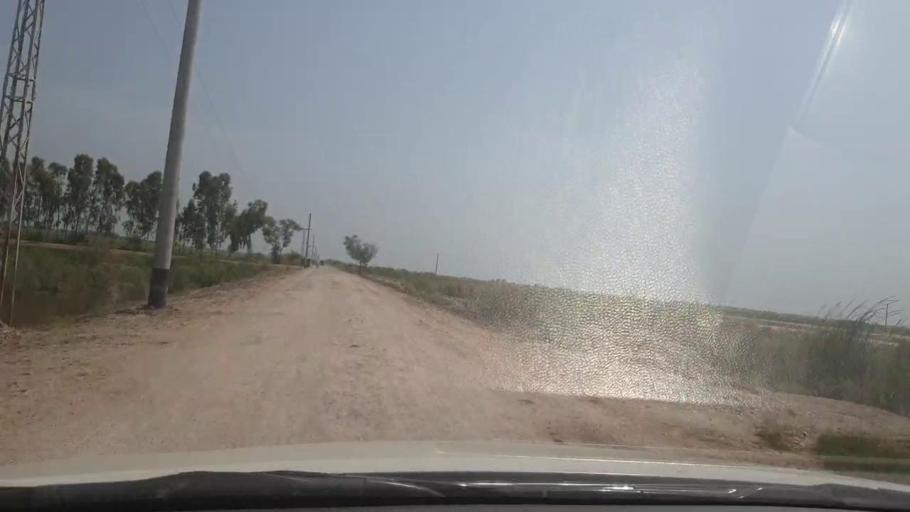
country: PK
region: Sindh
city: Garhi Yasin
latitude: 27.9575
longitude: 68.5052
